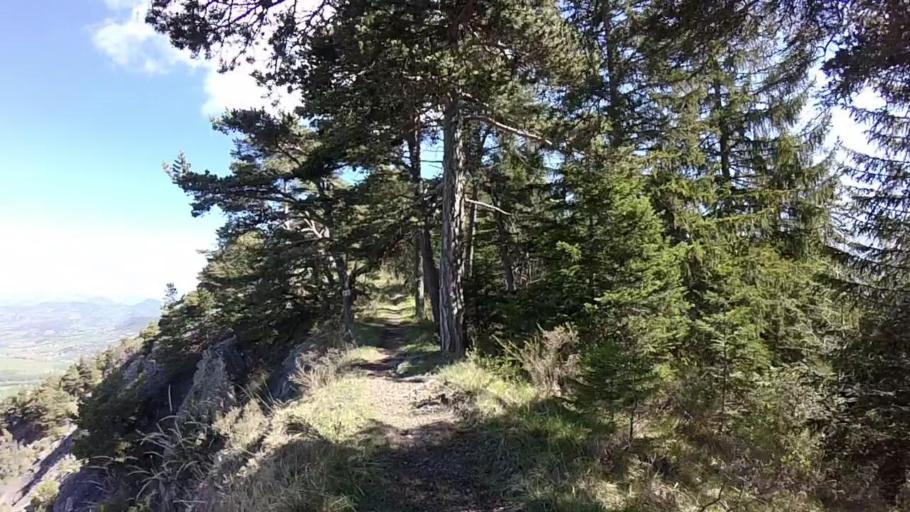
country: FR
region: Provence-Alpes-Cote d'Azur
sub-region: Departement des Alpes-de-Haute-Provence
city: Seyne-les-Alpes
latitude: 44.3206
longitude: 6.3738
